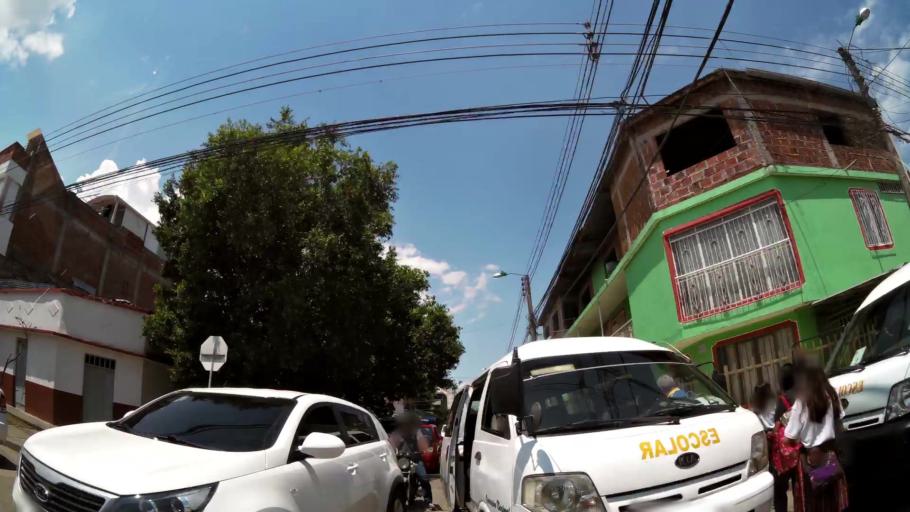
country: CO
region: Valle del Cauca
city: Cali
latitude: 3.4478
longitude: -76.5006
